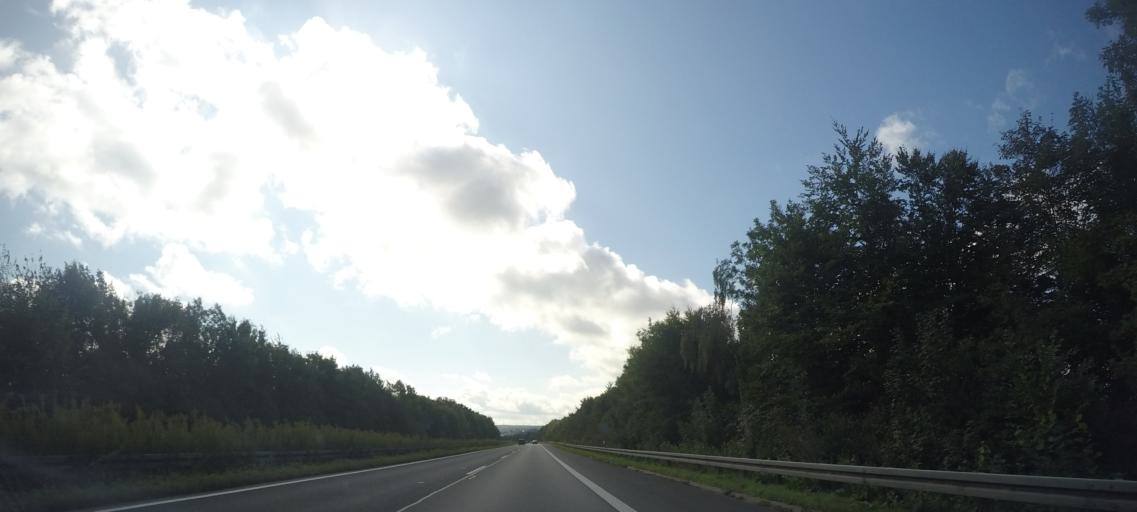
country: DE
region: North Rhine-Westphalia
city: Wickede
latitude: 51.4836
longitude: 7.9280
